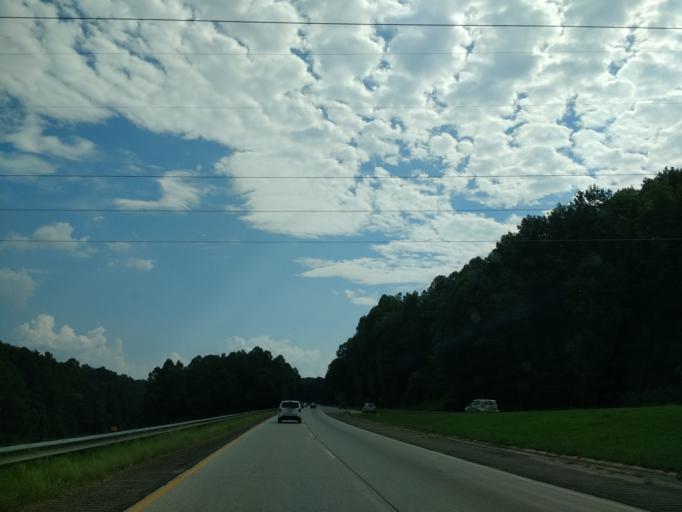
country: US
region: Georgia
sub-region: Hall County
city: Gainesville
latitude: 34.2810
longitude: -83.8087
